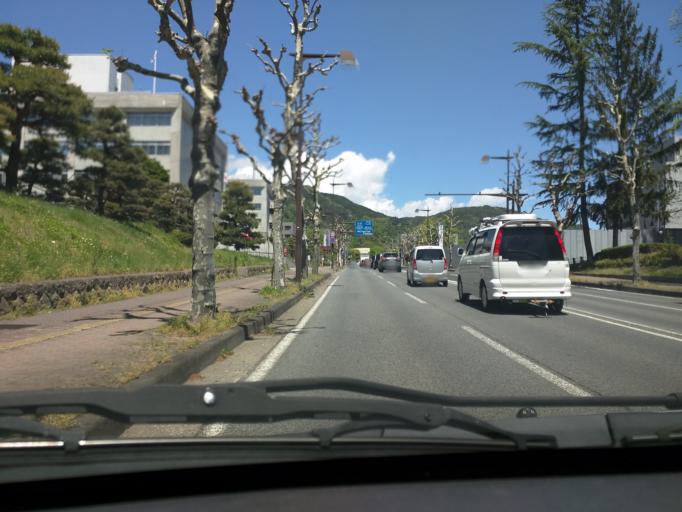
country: JP
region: Nagano
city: Nagano-shi
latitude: 36.6544
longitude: 138.1817
